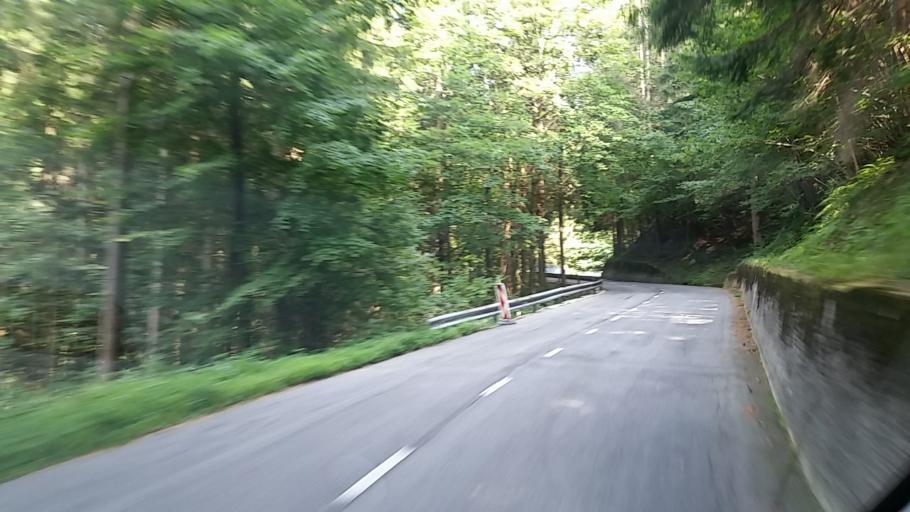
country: SI
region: Bohinj
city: Bohinjska Bistrica
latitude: 46.2127
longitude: 13.9902
